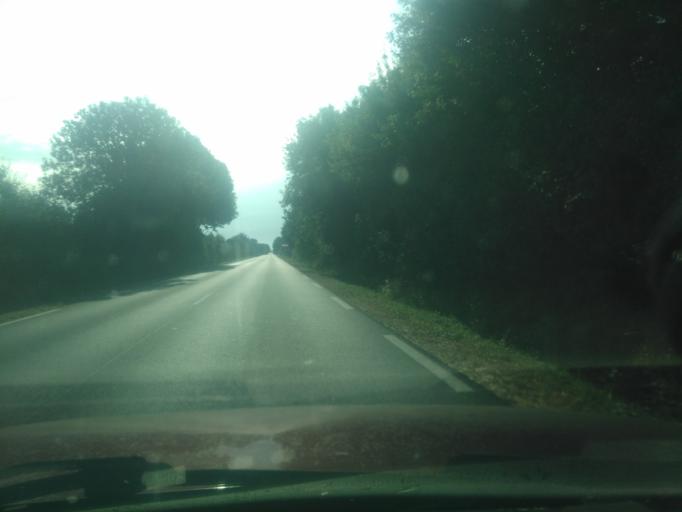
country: FR
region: Pays de la Loire
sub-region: Departement de la Vendee
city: Bazoges-en-Pareds
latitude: 46.6796
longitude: -0.9493
